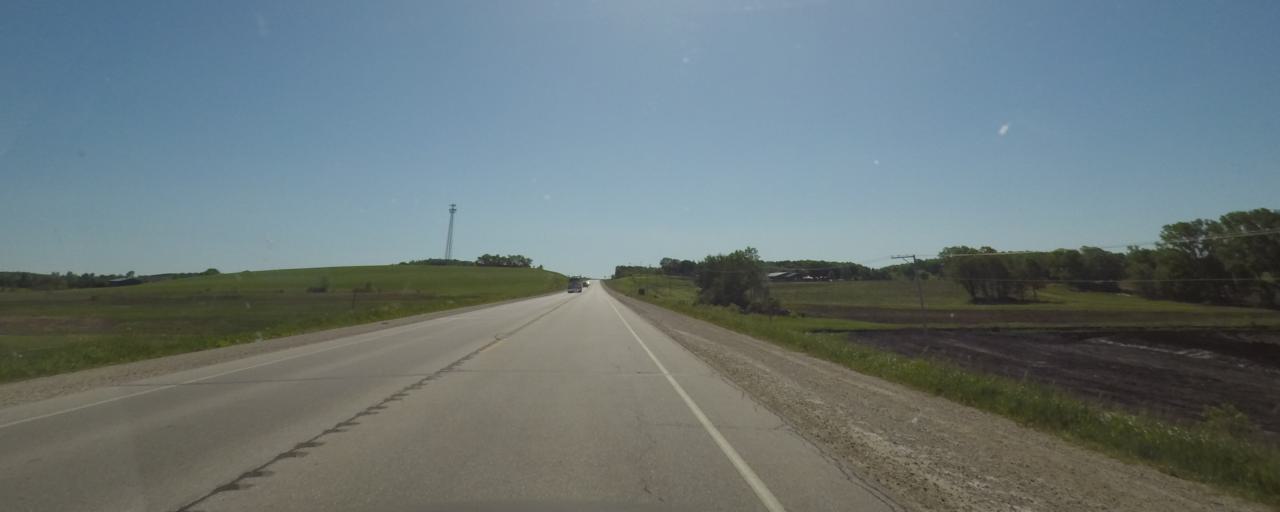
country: US
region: Wisconsin
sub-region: Fond du Lac County
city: Saint Peter
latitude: 43.7832
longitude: -88.3096
